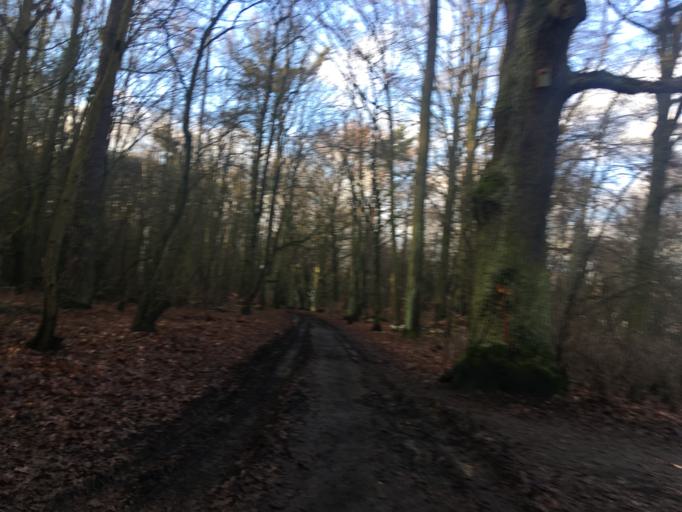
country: DE
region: Berlin
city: Waidmannslust
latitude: 52.6000
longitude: 13.3143
